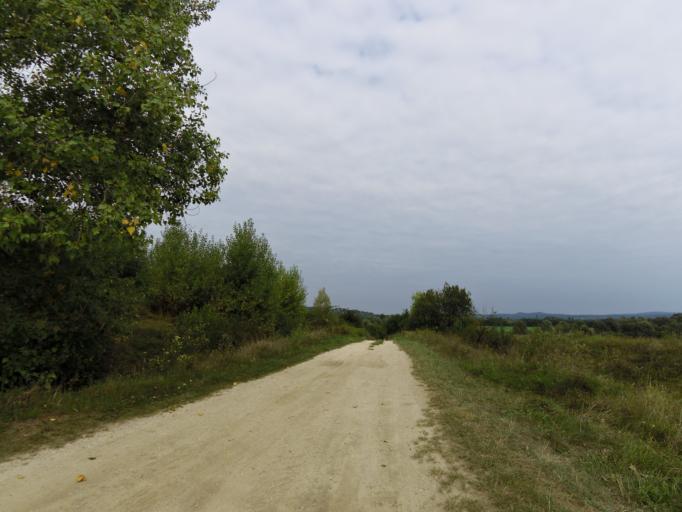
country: HU
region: Veszprem
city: Tapolca
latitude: 46.8373
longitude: 17.3682
